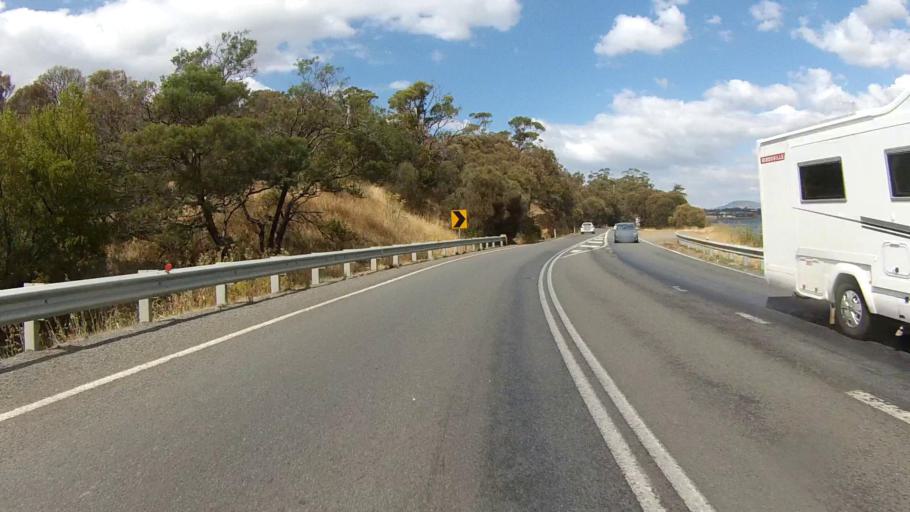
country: AU
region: Tasmania
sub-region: Brighton
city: Old Beach
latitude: -42.7780
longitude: 147.2845
